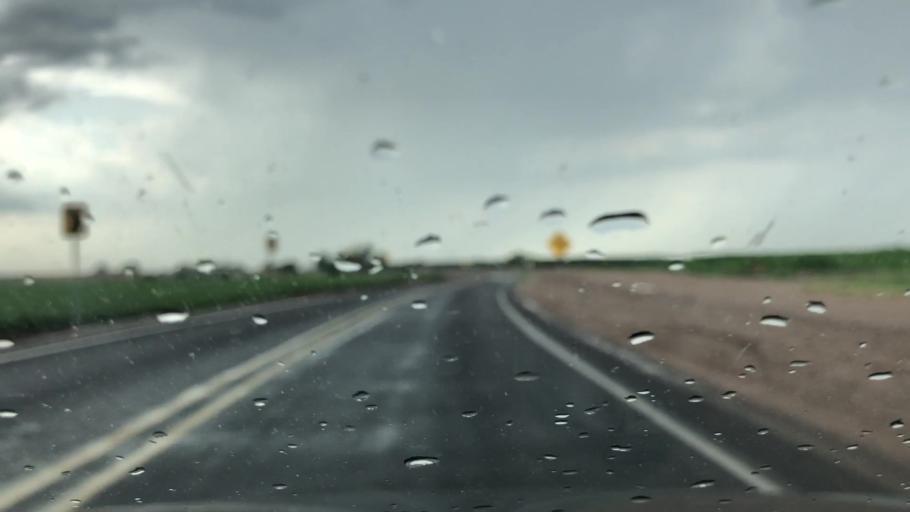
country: US
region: New Mexico
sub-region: Dona Ana County
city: Vado
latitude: 32.0657
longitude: -106.6793
